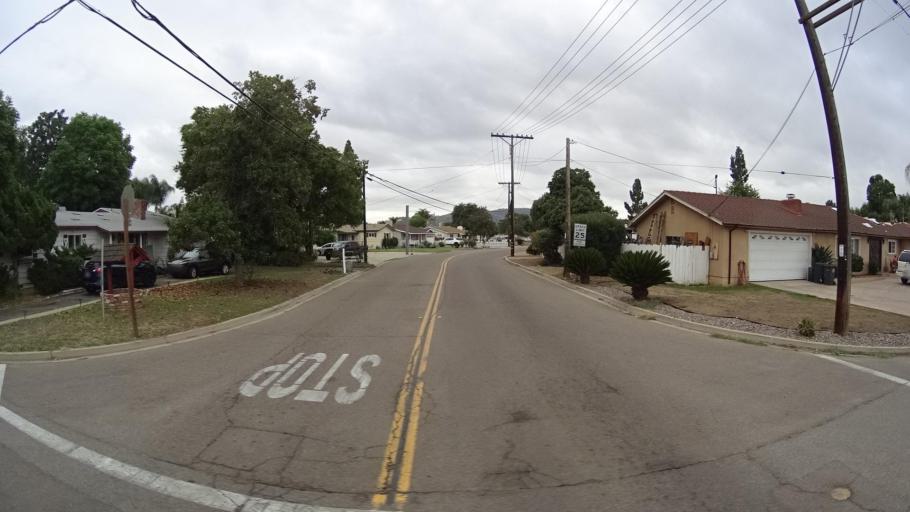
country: US
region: California
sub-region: San Diego County
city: Eucalyptus Hills
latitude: 32.8671
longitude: -116.9389
